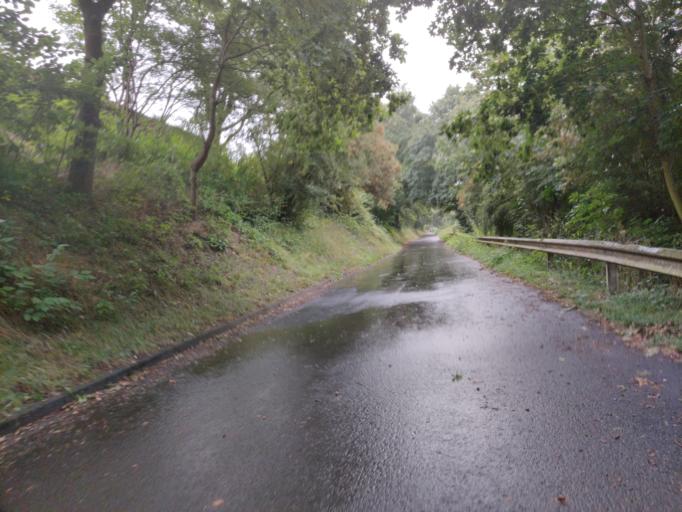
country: DE
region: Lower Saxony
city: Bad Karlshafen
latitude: 51.6481
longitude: 9.4394
